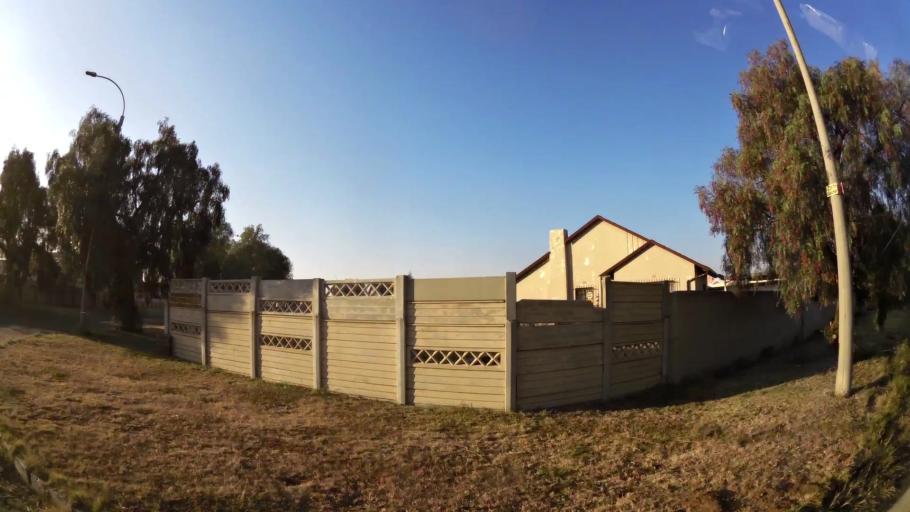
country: ZA
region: Gauteng
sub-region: West Rand District Municipality
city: Randfontein
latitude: -26.2099
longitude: 27.6531
